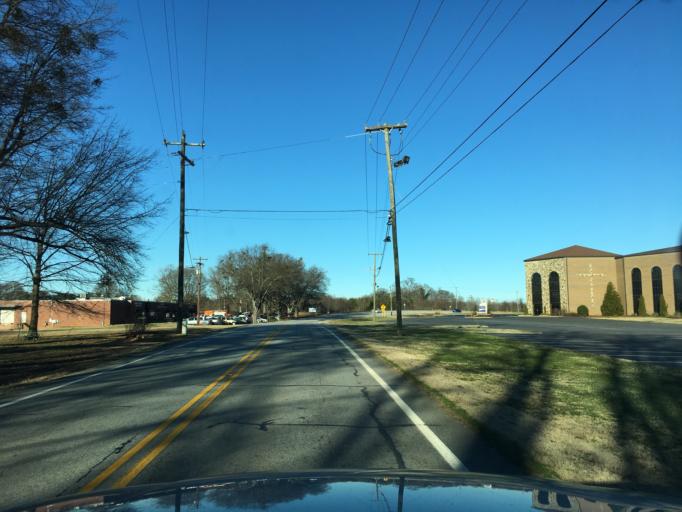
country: US
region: South Carolina
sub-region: Greenville County
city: Greer
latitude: 34.9250
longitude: -82.2492
